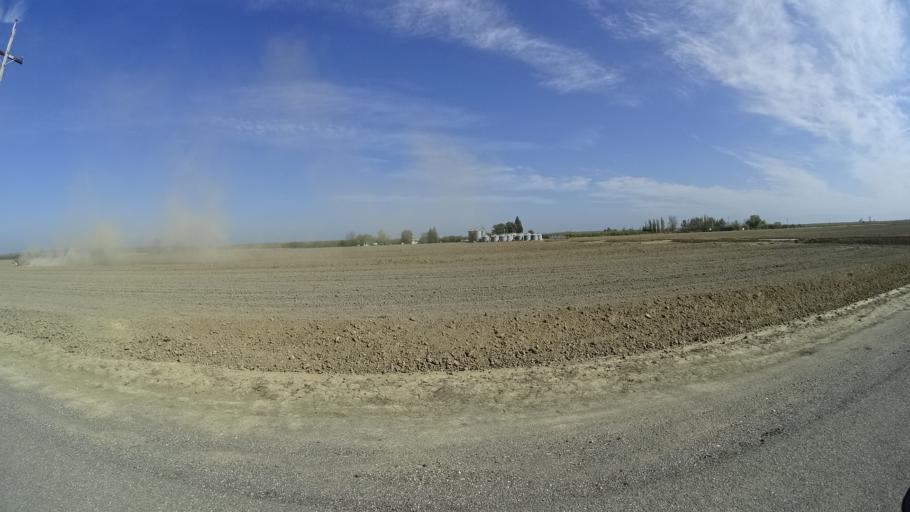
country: US
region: California
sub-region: Glenn County
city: Hamilton City
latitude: 39.6232
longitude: -122.0419
